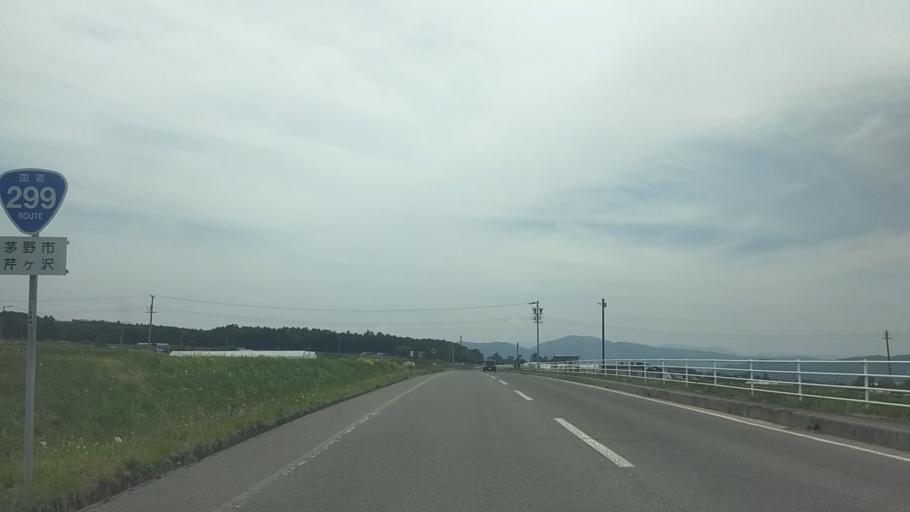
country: JP
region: Nagano
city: Chino
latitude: 36.0288
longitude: 138.2381
